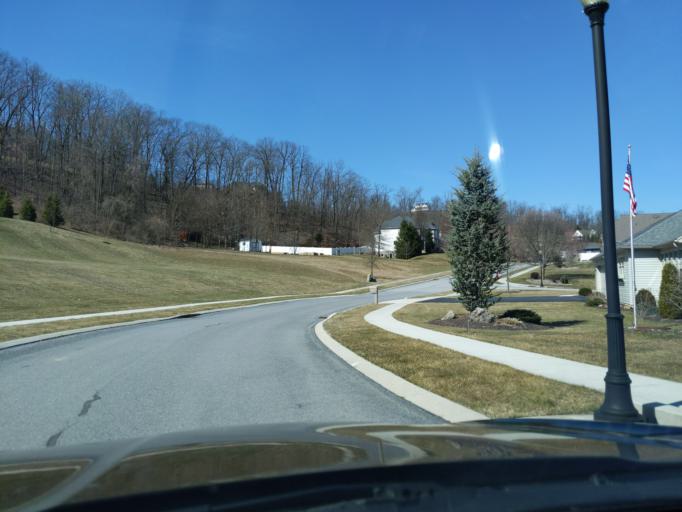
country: US
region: Pennsylvania
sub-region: Blair County
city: Duncansville
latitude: 40.4099
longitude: -78.4207
